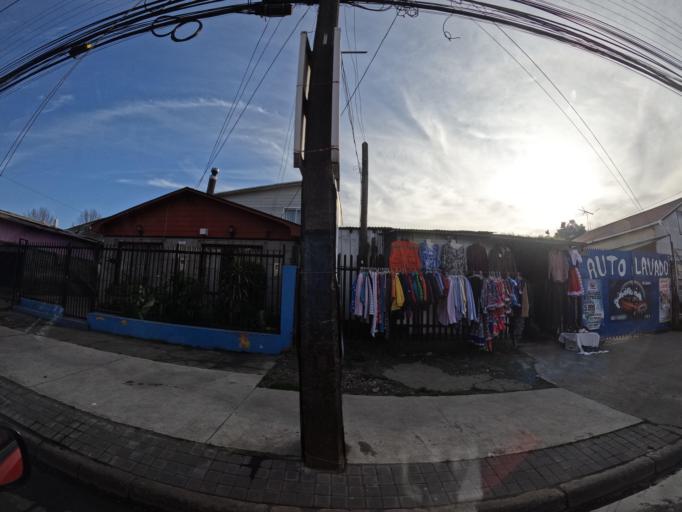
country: CL
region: Biobio
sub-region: Provincia de Concepcion
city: Concepcion
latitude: -36.7934
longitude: -73.0455
